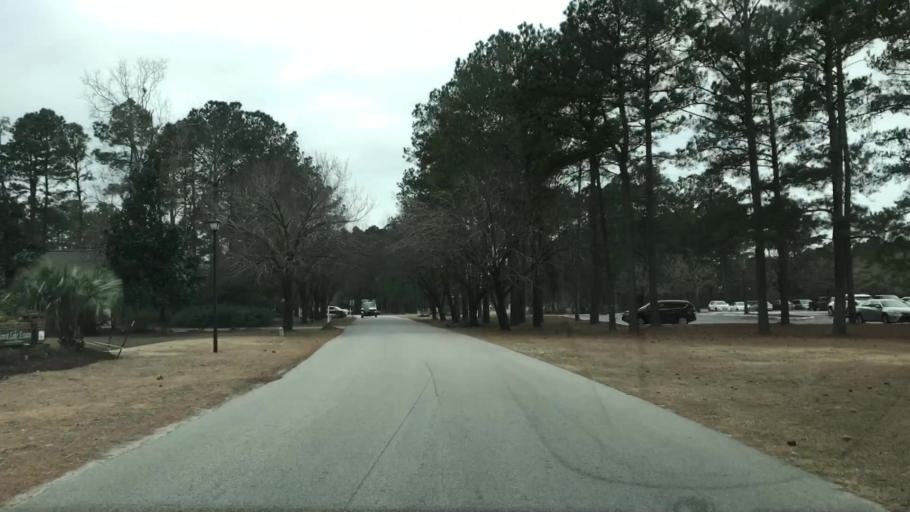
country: US
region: South Carolina
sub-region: Horry County
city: Red Hill
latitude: 33.7759
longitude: -79.0026
